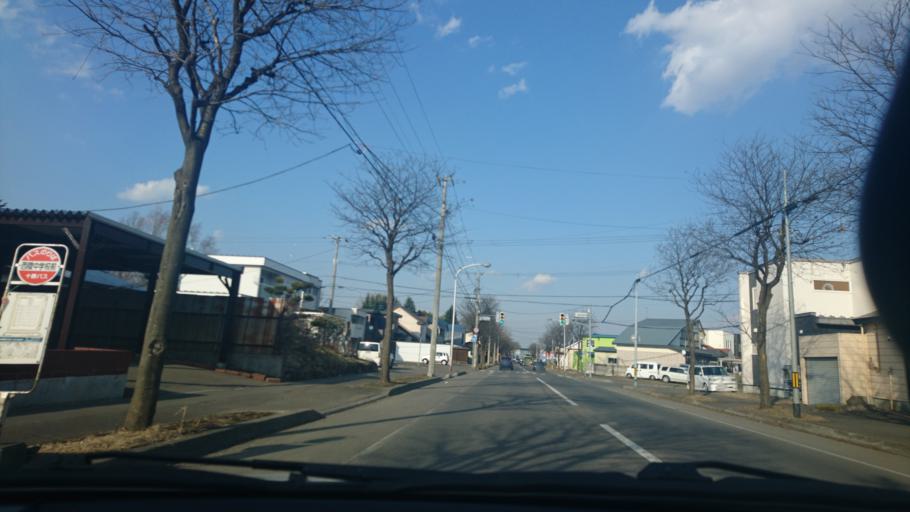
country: JP
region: Hokkaido
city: Obihiro
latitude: 42.9237
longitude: 143.1590
